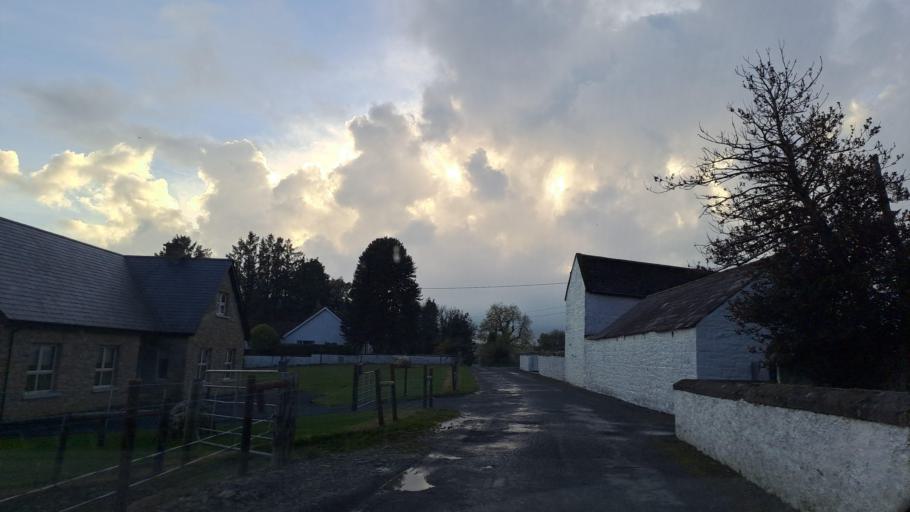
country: IE
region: Ulster
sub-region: County Monaghan
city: Carrickmacross
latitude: 53.9740
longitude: -6.7506
